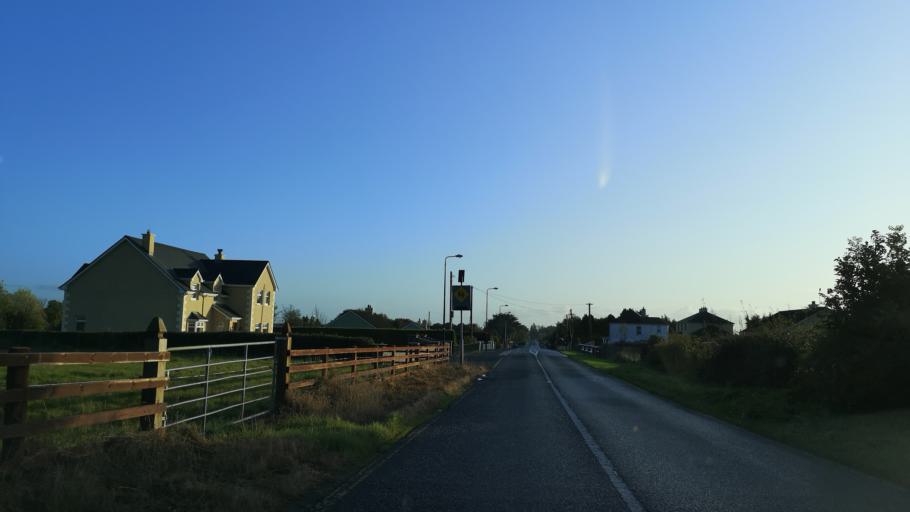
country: IE
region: Connaught
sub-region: Roscommon
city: Castlerea
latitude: 53.7349
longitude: -8.5514
